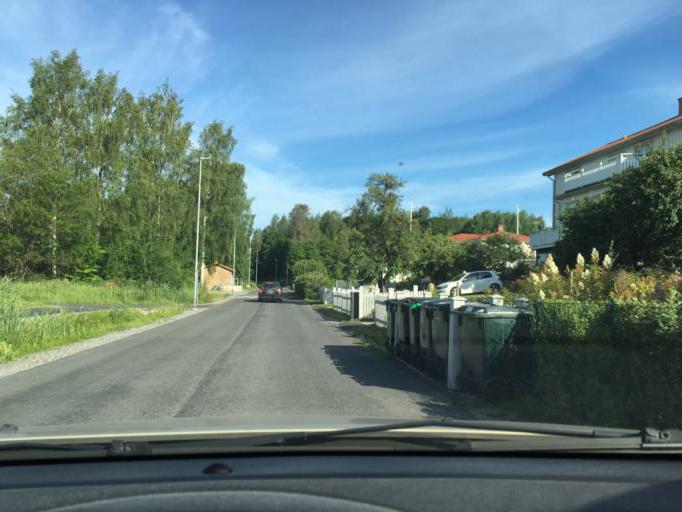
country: SE
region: Stockholm
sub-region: Sodertalje Kommun
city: Pershagen
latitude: 59.1849
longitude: 17.6539
